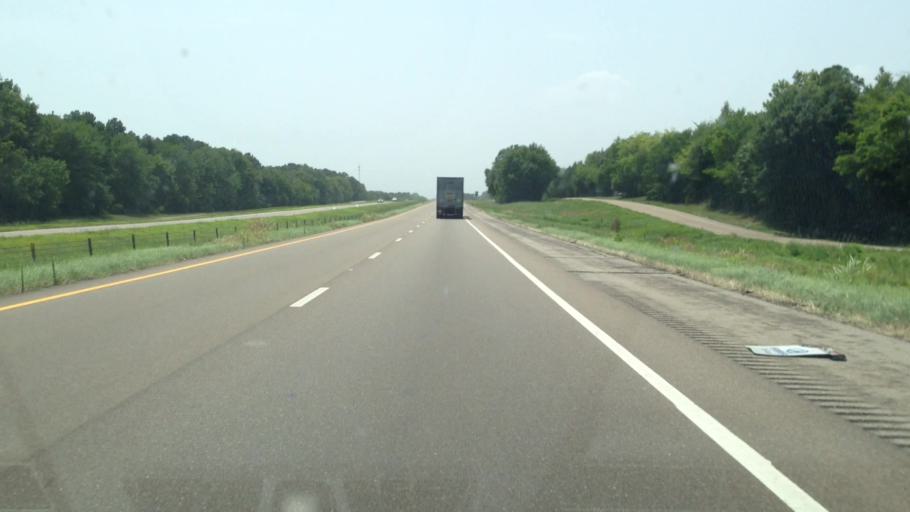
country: US
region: Texas
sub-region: Titus County
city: Mount Pleasant
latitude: 33.1596
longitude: -95.0801
